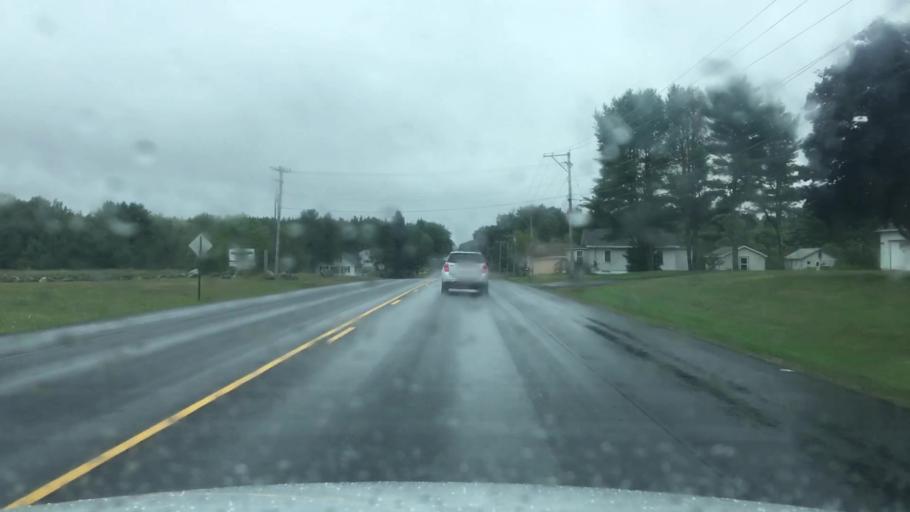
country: US
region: Maine
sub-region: Penobscot County
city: Hampden
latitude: 44.7659
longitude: -68.8535
